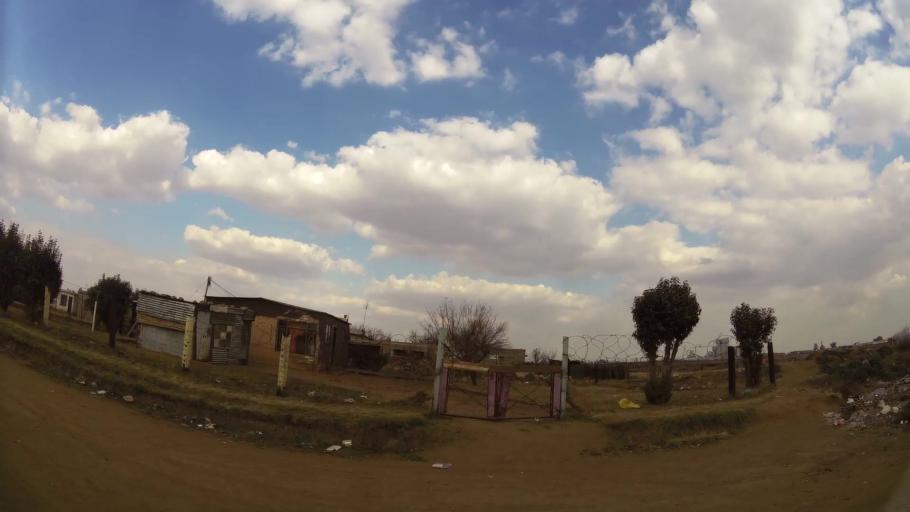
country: ZA
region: Mpumalanga
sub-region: Nkangala District Municipality
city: Delmas
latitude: -26.1424
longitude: 28.6954
